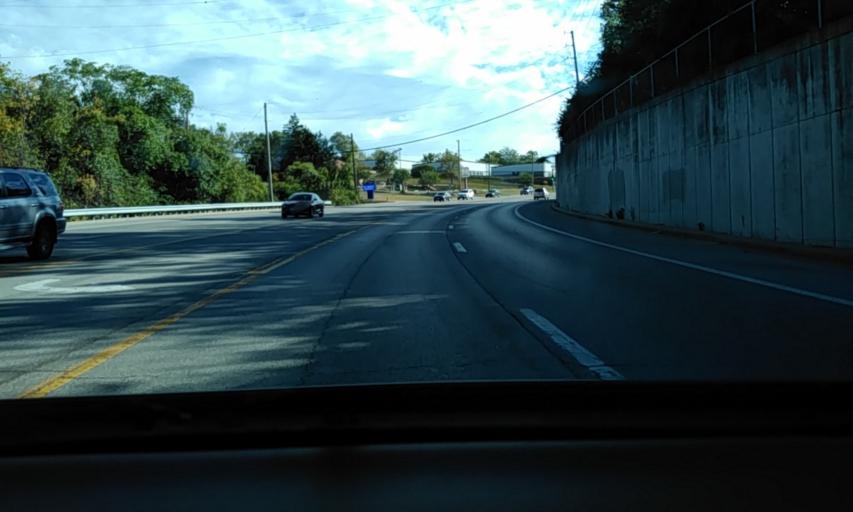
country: US
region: Missouri
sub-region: Saint Louis County
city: Mehlville
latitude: 38.4981
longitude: -90.3408
